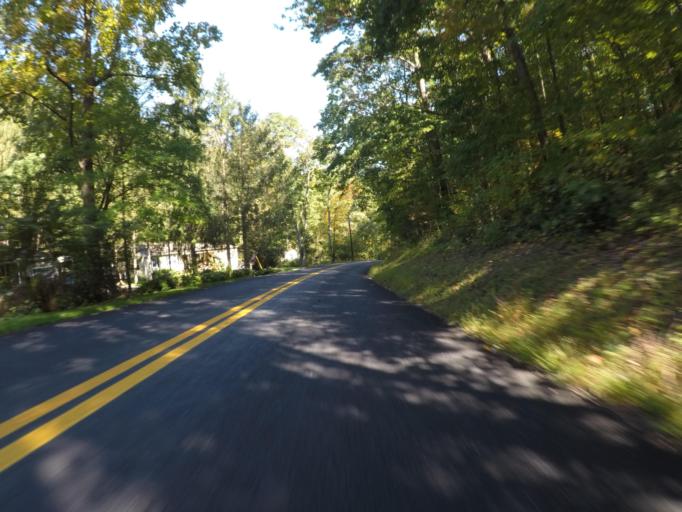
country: US
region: Maryland
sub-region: Carroll County
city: Hampstead
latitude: 39.5873
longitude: -76.9029
